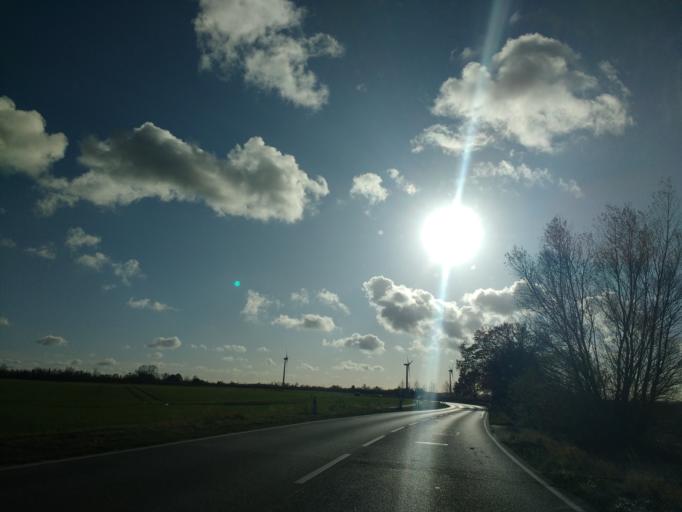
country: DE
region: Mecklenburg-Vorpommern
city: Grevesmuhlen
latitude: 53.8390
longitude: 11.2083
